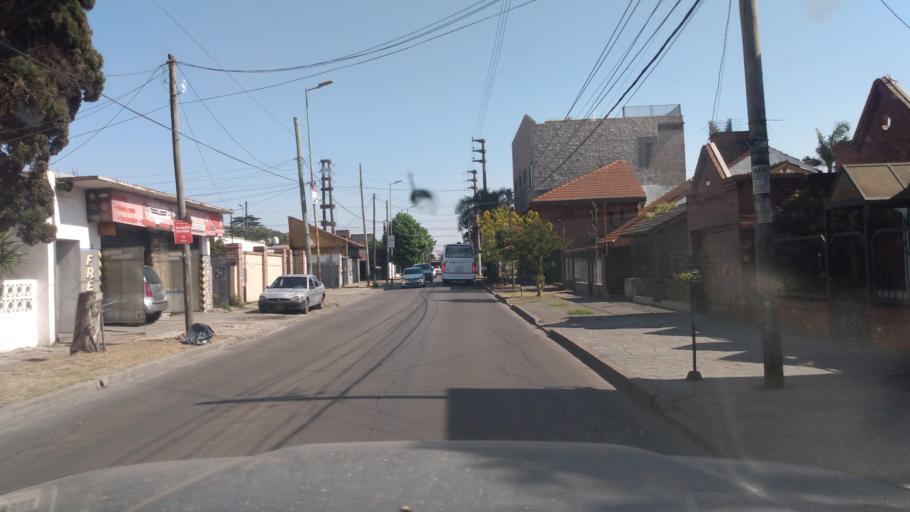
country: AR
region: Buenos Aires
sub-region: Partido de Moron
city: Moron
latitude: -34.6343
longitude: -58.5984
